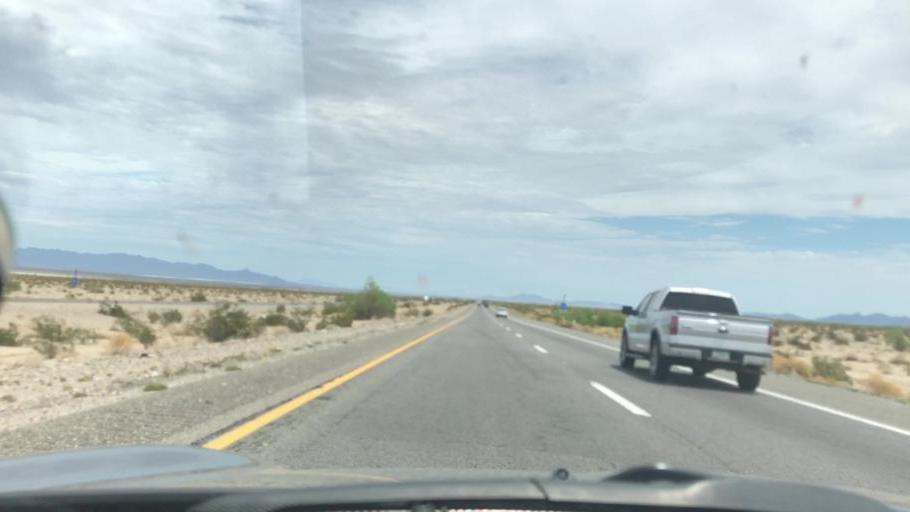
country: US
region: California
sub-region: Riverside County
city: Mesa Verde
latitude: 33.6699
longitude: -115.2022
